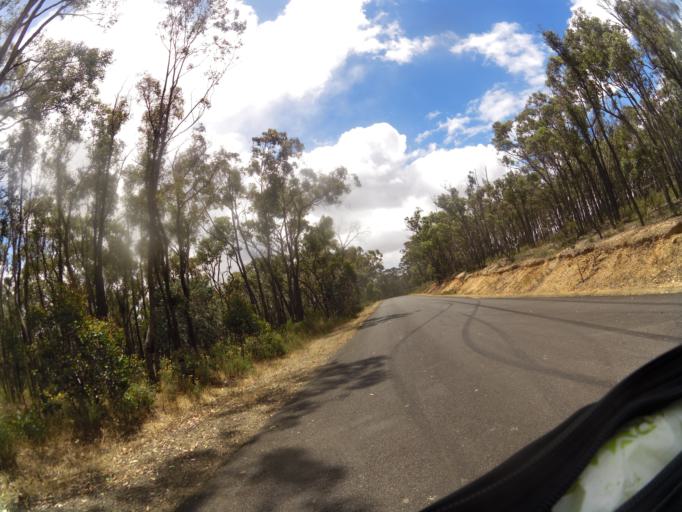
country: AU
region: Victoria
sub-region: Mount Alexander
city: Castlemaine
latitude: -37.0213
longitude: 144.2439
